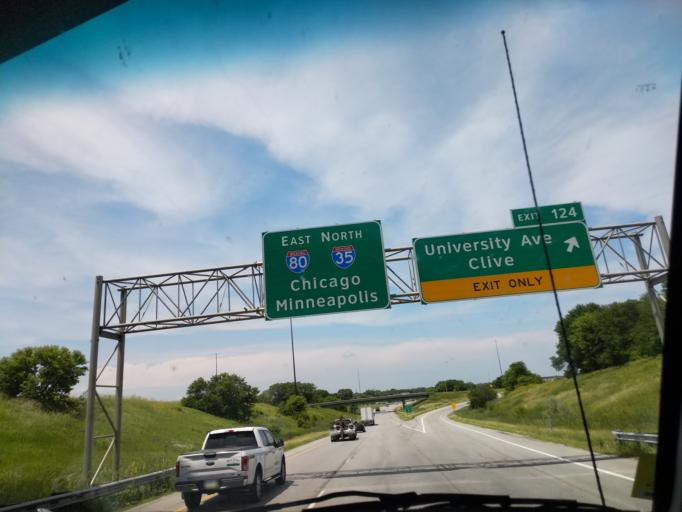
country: US
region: Iowa
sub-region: Polk County
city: Clive
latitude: 41.5953
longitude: -93.7745
